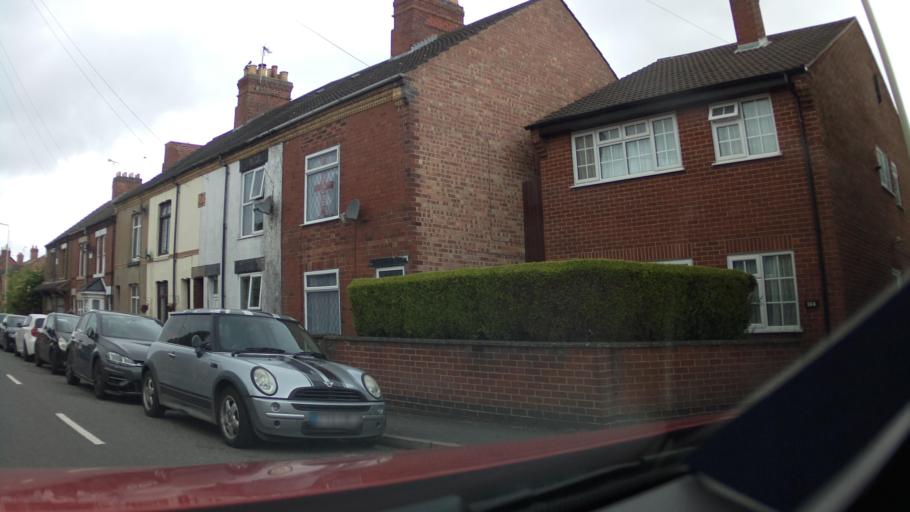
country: GB
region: England
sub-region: Leicestershire
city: Coalville
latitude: 52.7330
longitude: -1.3637
